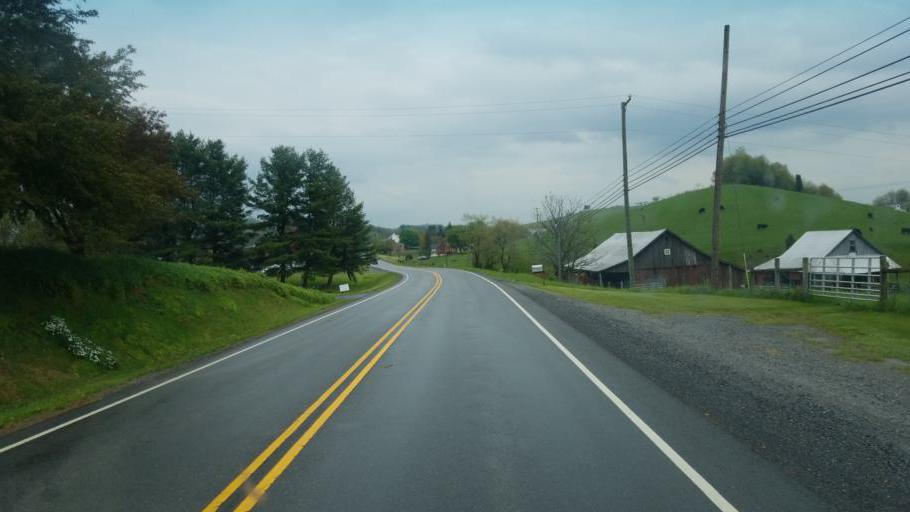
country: US
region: Virginia
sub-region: Wythe County
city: Rural Retreat
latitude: 36.8925
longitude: -81.3452
